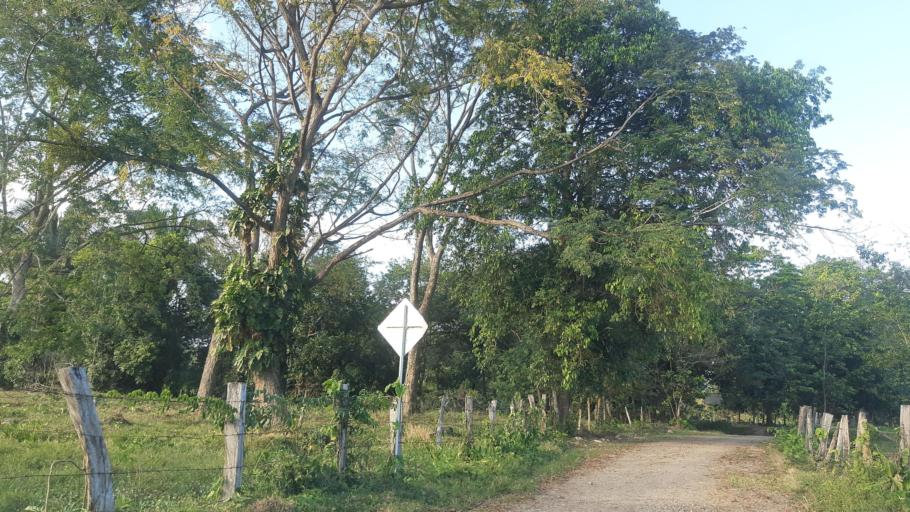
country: CO
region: Arauca
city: Tame
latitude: 6.4982
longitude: -71.7677
